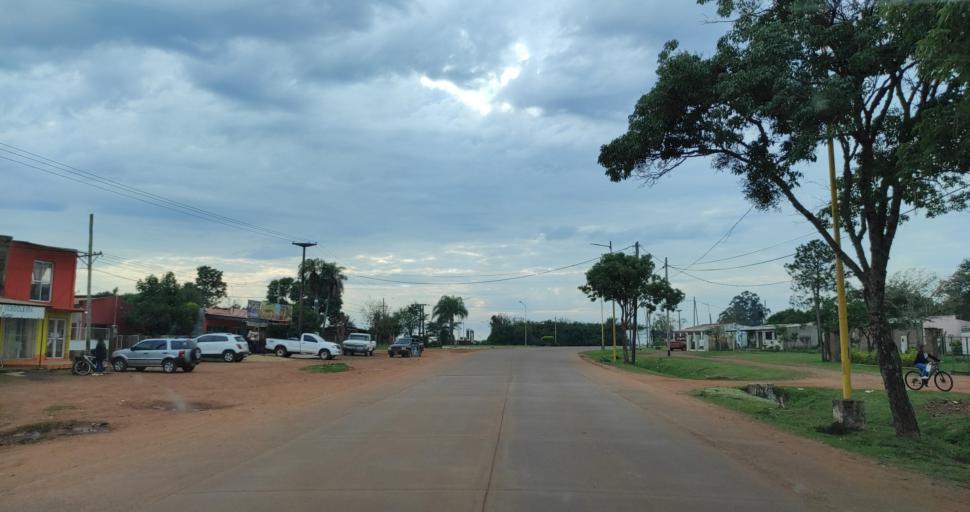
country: AR
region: Corrientes
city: Santo Tome
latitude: -28.5475
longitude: -56.0627
